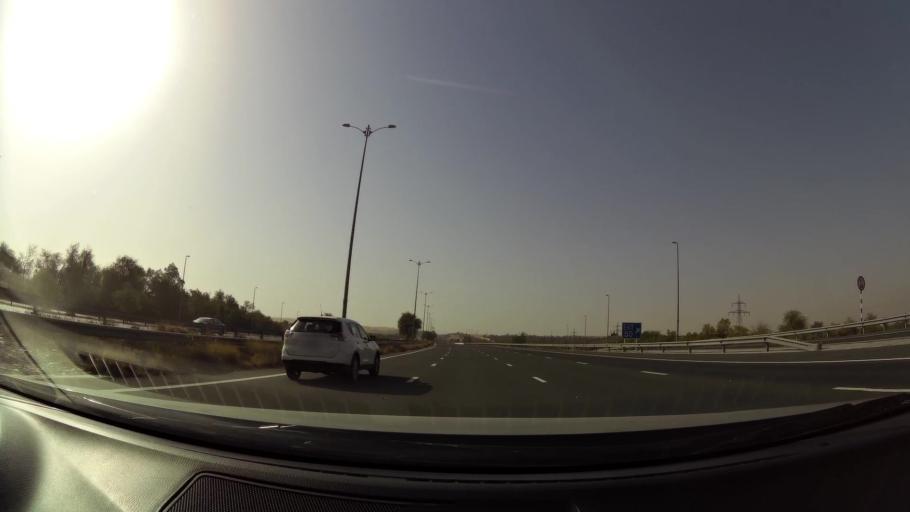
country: OM
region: Al Buraimi
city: Al Buraymi
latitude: 24.6428
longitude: 55.7080
